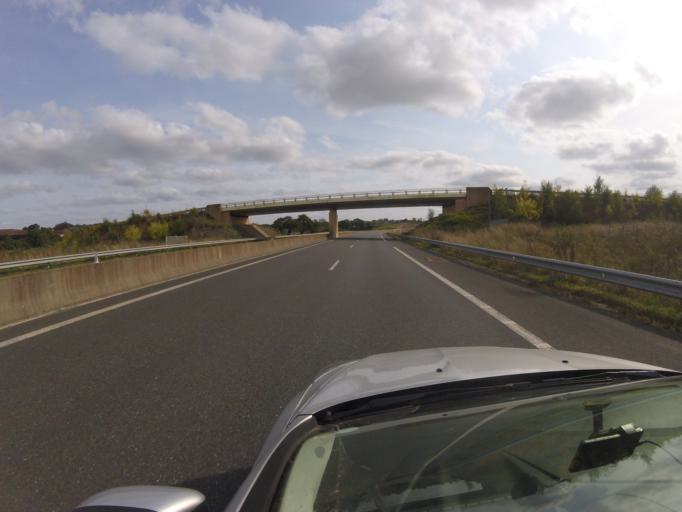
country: FR
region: Lower Normandy
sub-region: Departement de la Manche
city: La Meauffe
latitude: 49.2330
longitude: -1.1263
